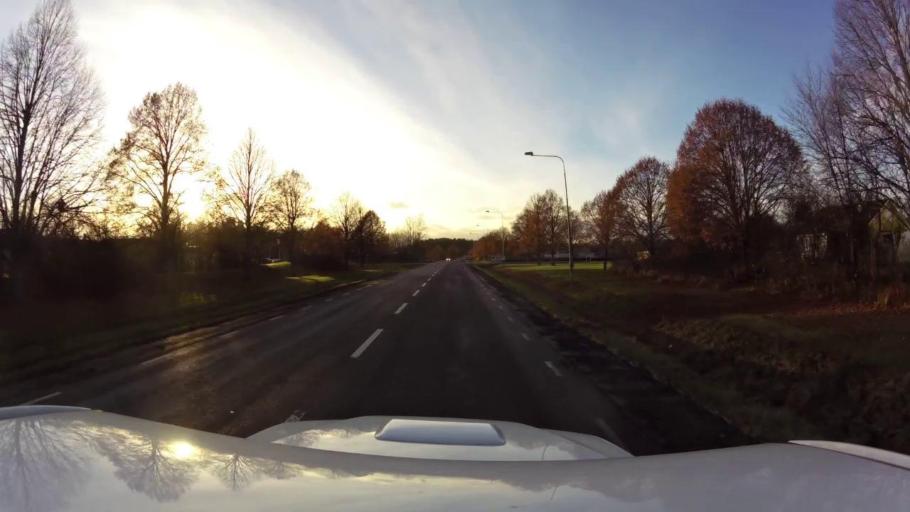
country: SE
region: OEstergoetland
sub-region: Linkopings Kommun
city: Linkoping
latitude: 58.3837
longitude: 15.6529
